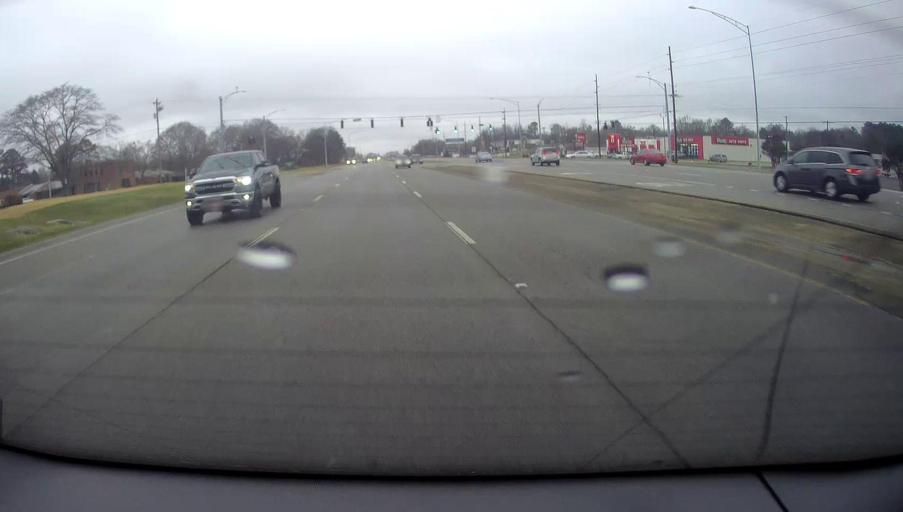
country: US
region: Alabama
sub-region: Morgan County
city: Decatur
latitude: 34.5830
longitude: -87.0233
